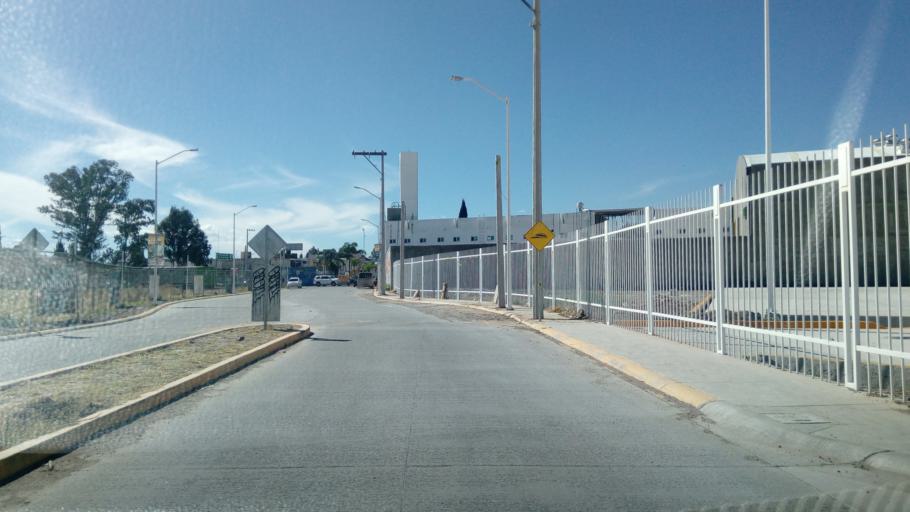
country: MX
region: Durango
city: Victoria de Durango
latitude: 24.0459
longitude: -104.6308
